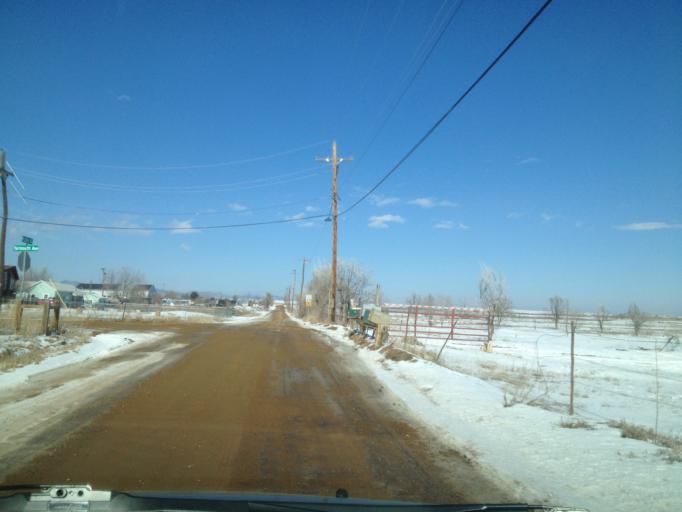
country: US
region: Colorado
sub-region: Boulder County
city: Boulder
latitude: 40.0580
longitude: -105.2634
